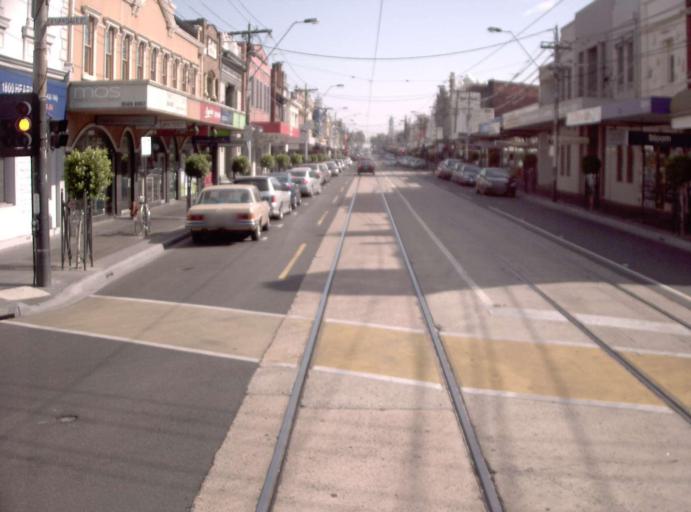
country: AU
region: Victoria
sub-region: Glen Eira
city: Caulfield North
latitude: -37.8644
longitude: 145.0280
